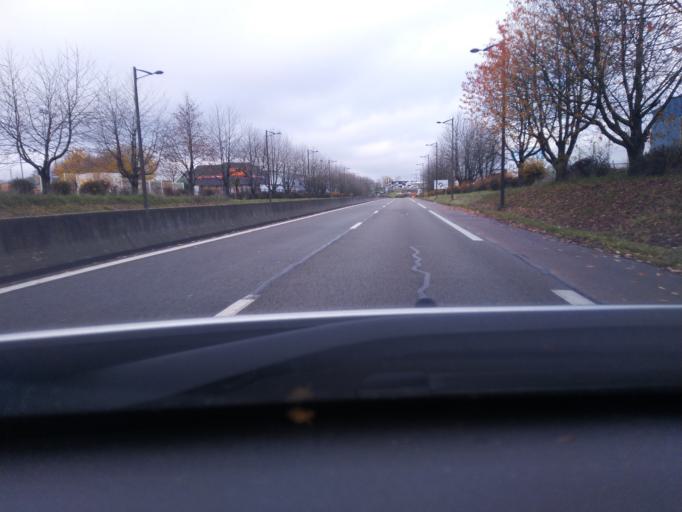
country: FR
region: Haute-Normandie
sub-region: Departement de la Seine-Maritime
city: Maromme
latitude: 49.4859
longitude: 1.0162
